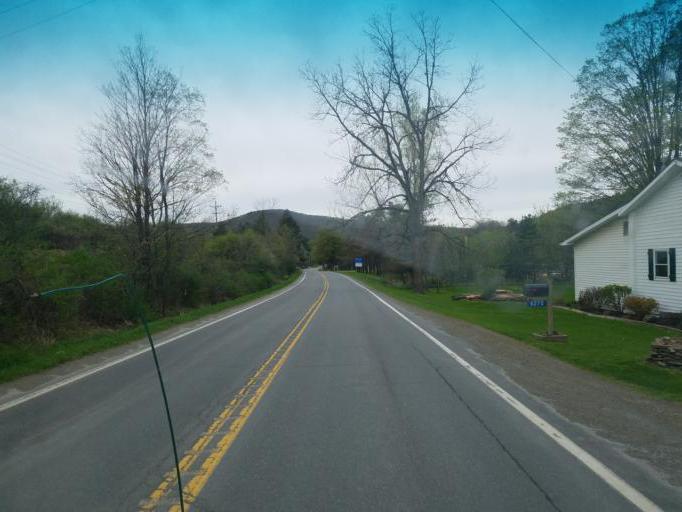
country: US
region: Pennsylvania
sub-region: Tioga County
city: Westfield
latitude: 41.9081
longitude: -77.5346
